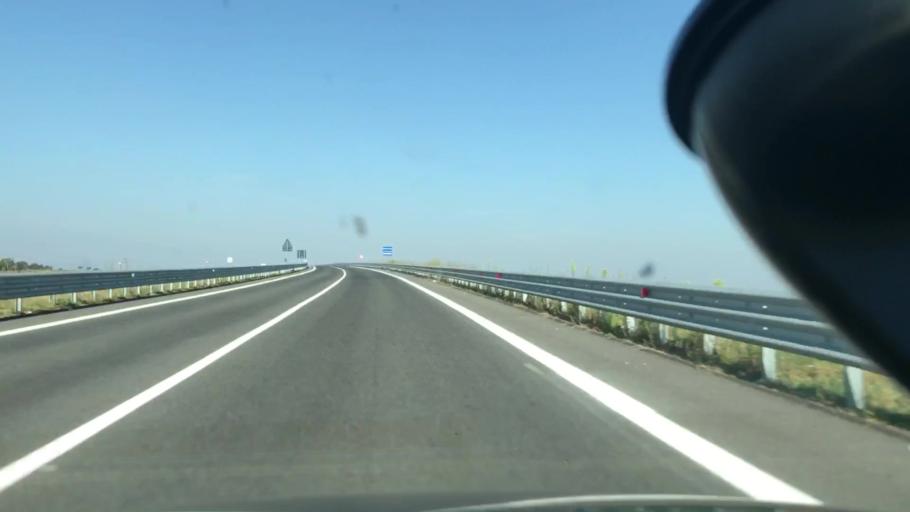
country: IT
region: Basilicate
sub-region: Provincia di Potenza
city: Palazzo San Gervasio
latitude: 40.9698
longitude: 16.0009
